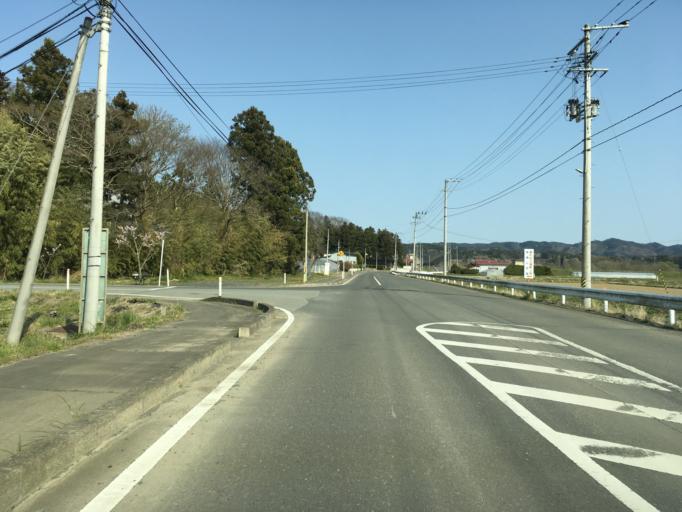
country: JP
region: Miyagi
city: Wakuya
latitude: 38.7202
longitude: 141.2767
